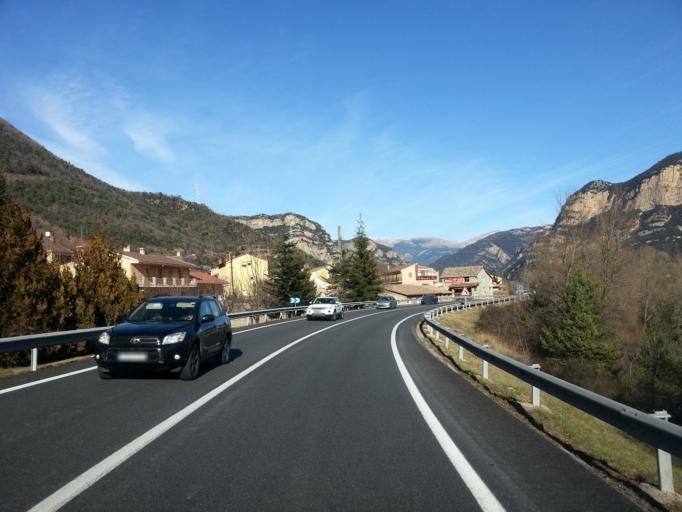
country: ES
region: Catalonia
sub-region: Provincia de Barcelona
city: Vallcebre
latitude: 42.1619
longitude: 1.8553
